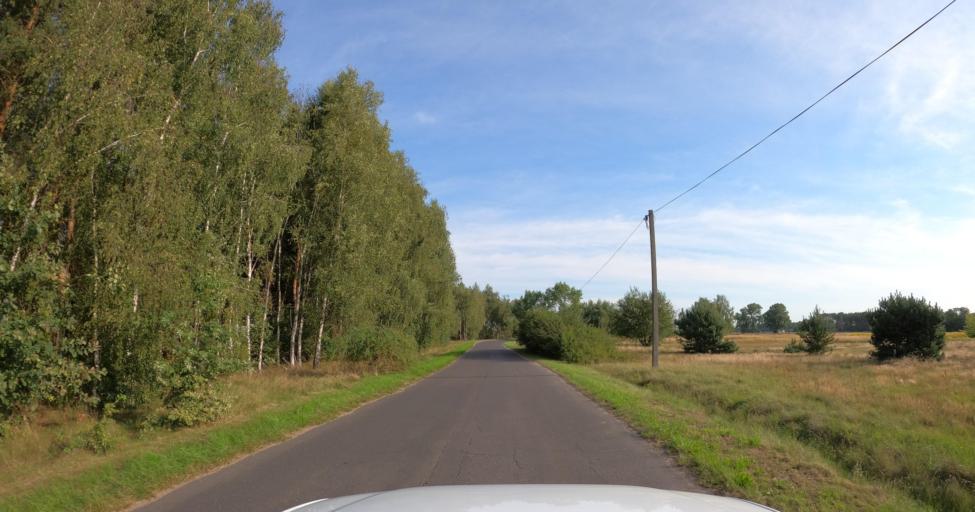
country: PL
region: West Pomeranian Voivodeship
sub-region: Powiat goleniowski
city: Goleniow
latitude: 53.5117
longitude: 14.7135
